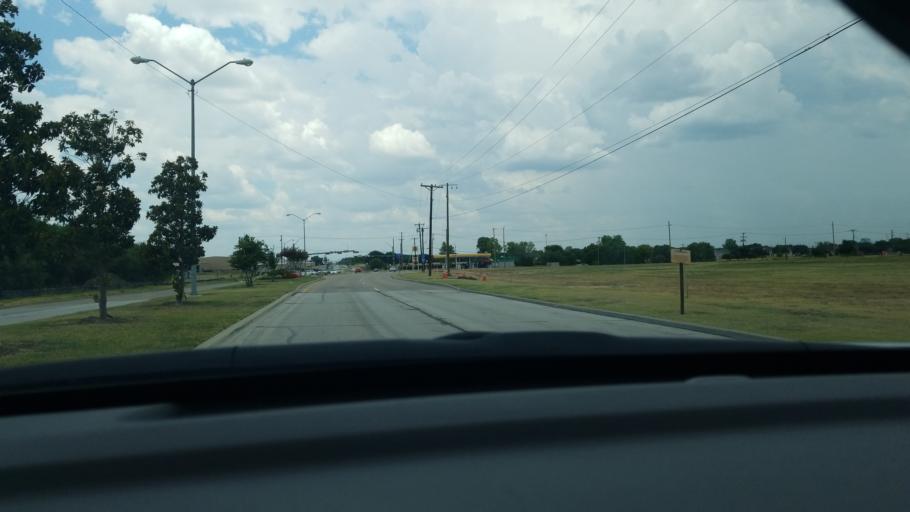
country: US
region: Texas
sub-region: Dallas County
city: Grand Prairie
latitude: 32.6892
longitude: -97.0442
